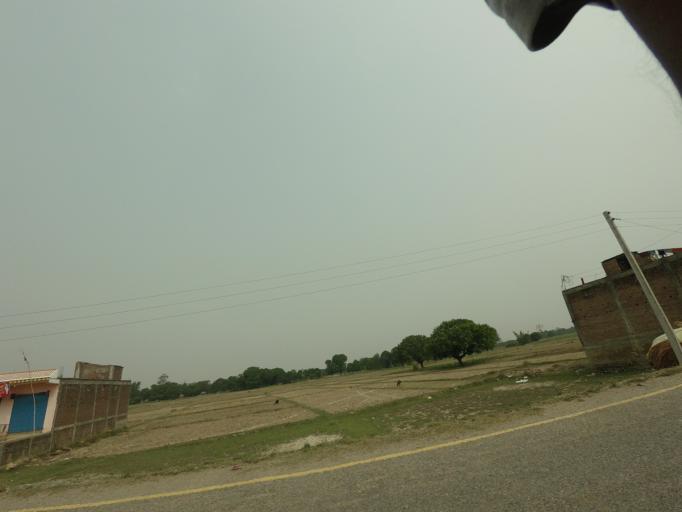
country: IN
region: Uttar Pradesh
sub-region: Maharajganj
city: Nautanwa
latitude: 27.4970
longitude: 83.3286
